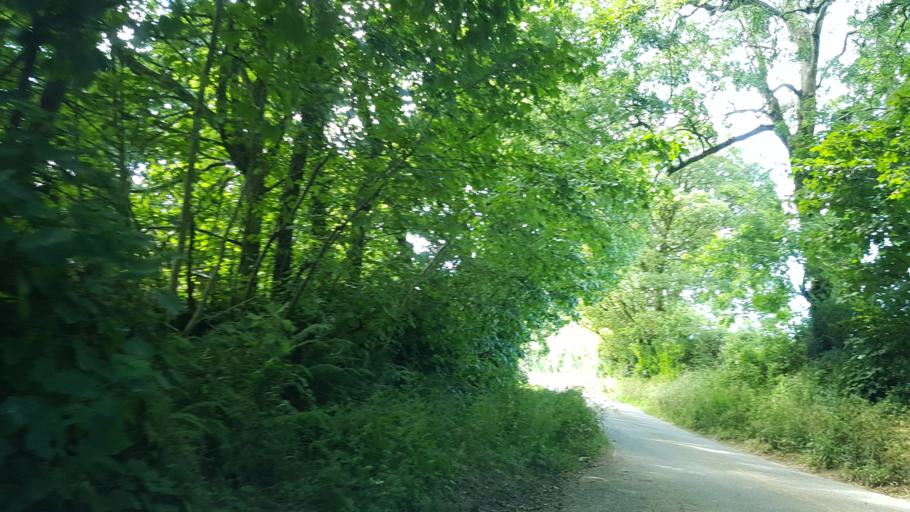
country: GB
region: Wales
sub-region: Pembrokeshire
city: Wiston
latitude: 51.8281
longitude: -4.8843
